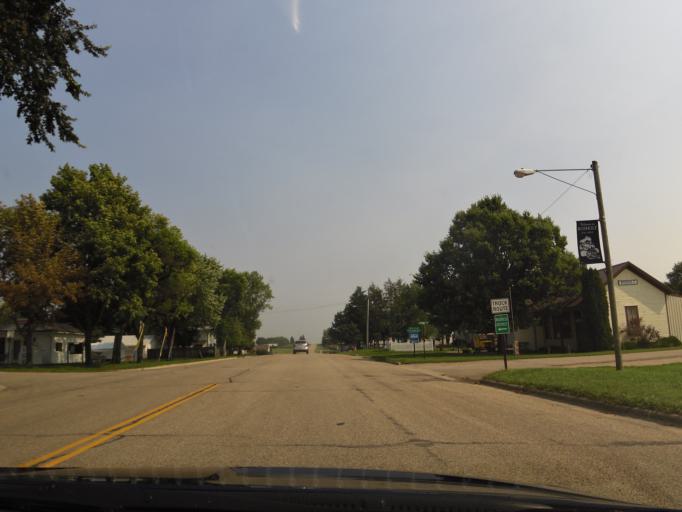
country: US
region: Minnesota
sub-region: Traverse County
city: Wheaton
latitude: 45.8635
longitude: -96.7334
